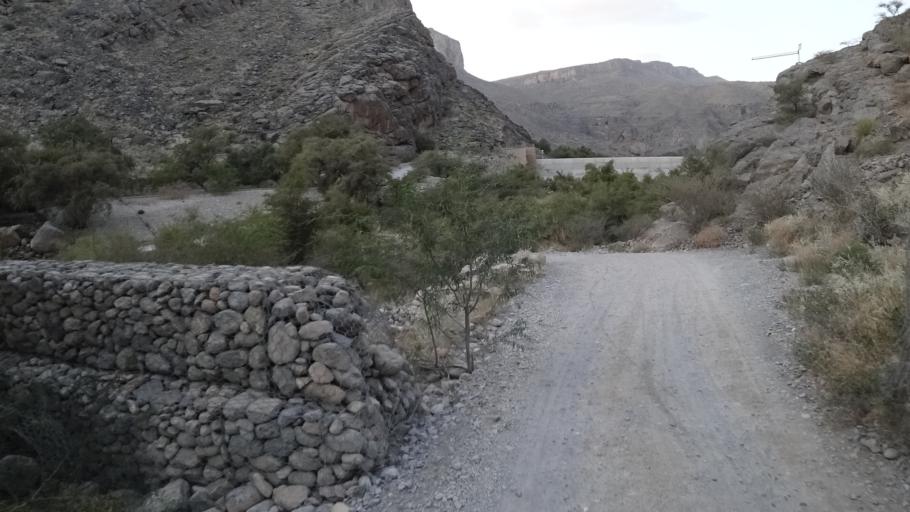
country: OM
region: Muhafazat ad Dakhiliyah
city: Nizwa
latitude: 23.0567
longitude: 57.4687
